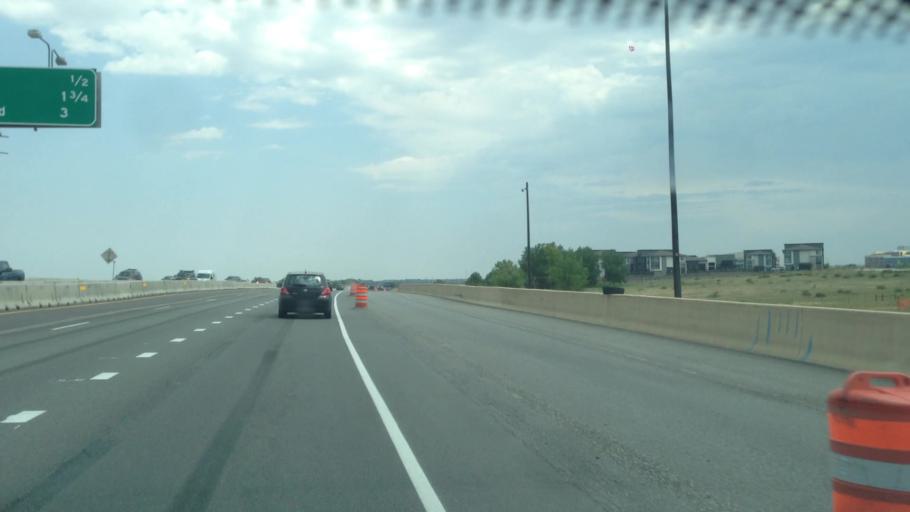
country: US
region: Colorado
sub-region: Arapahoe County
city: Columbine Valley
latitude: 39.5636
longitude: -105.0218
